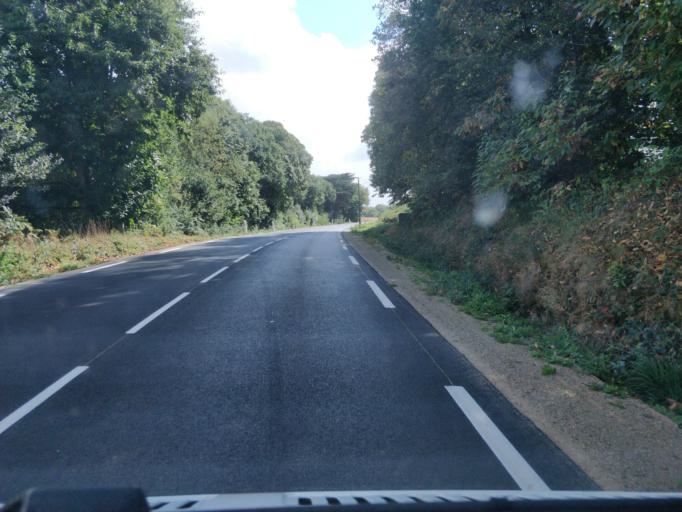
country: FR
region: Brittany
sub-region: Departement du Finistere
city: Landudec
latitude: 47.9999
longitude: -4.3228
